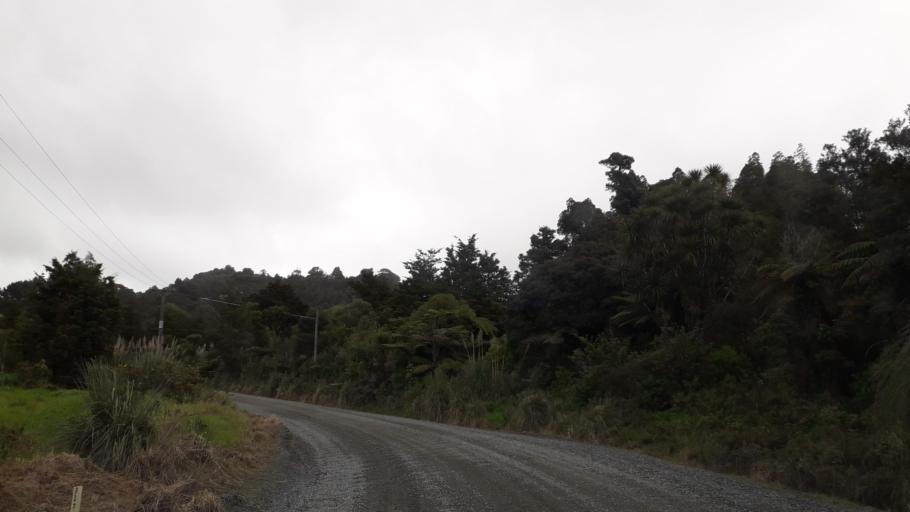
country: NZ
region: Northland
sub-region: Far North District
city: Kerikeri
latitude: -35.1172
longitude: 173.7519
